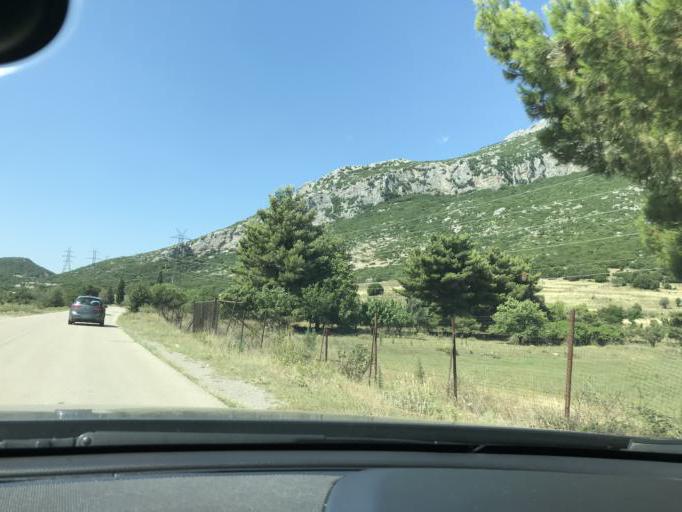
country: GR
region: Central Greece
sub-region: Nomos Voiotias
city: Distomo
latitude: 38.5069
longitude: 22.7056
